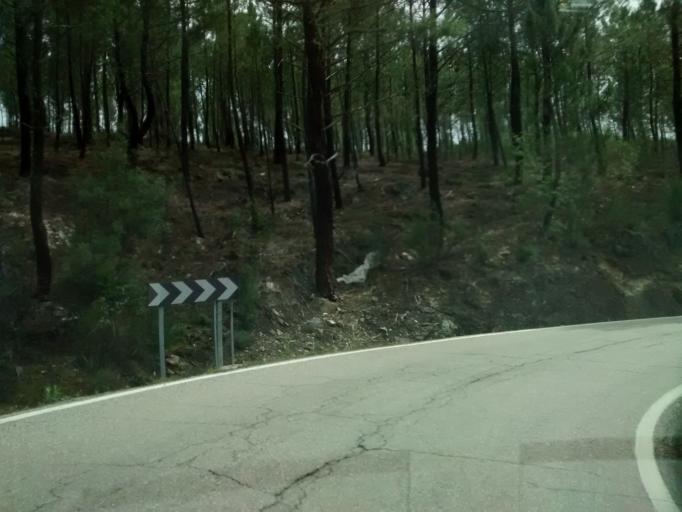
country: ES
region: Galicia
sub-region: Provincia de Ourense
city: Petin
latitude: 42.3448
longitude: -7.1795
